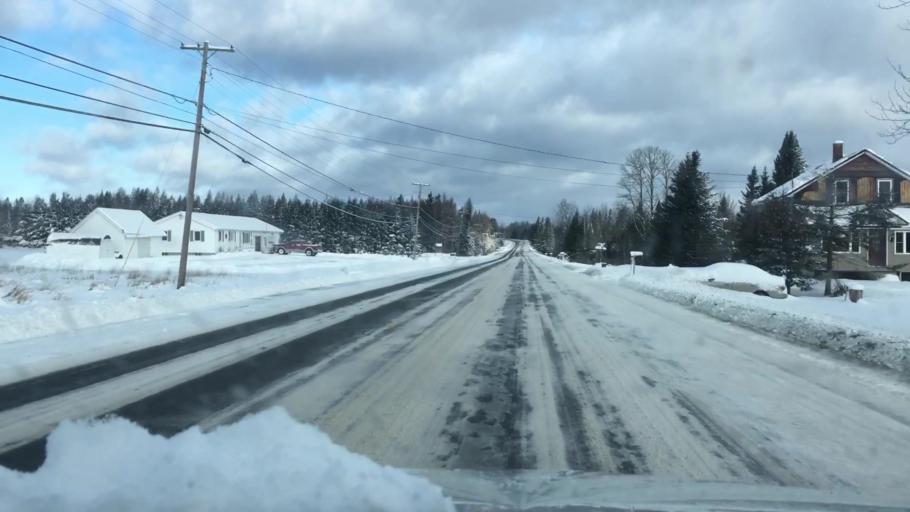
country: US
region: Maine
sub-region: Aroostook County
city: Caribou
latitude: 46.9174
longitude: -68.0188
